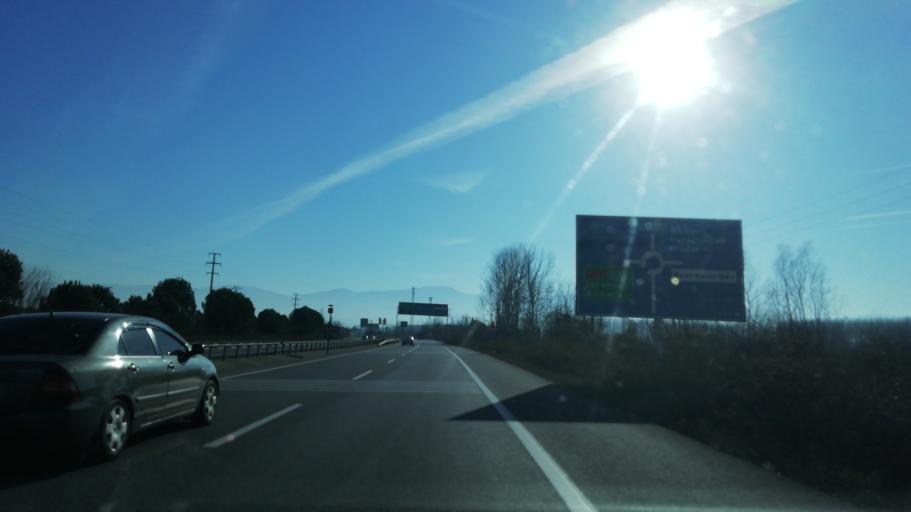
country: TR
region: Sakarya
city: Akyazi
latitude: 40.7247
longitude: 30.5633
